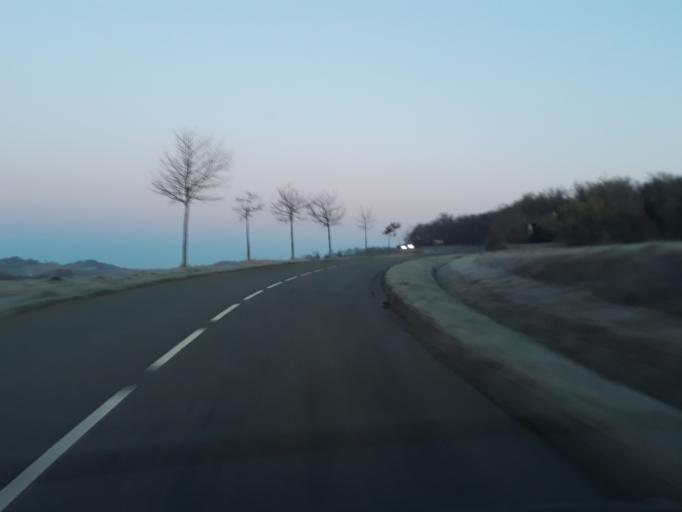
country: FR
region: Midi-Pyrenees
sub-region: Departement du Gers
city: Lombez
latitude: 43.5104
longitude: 0.8911
